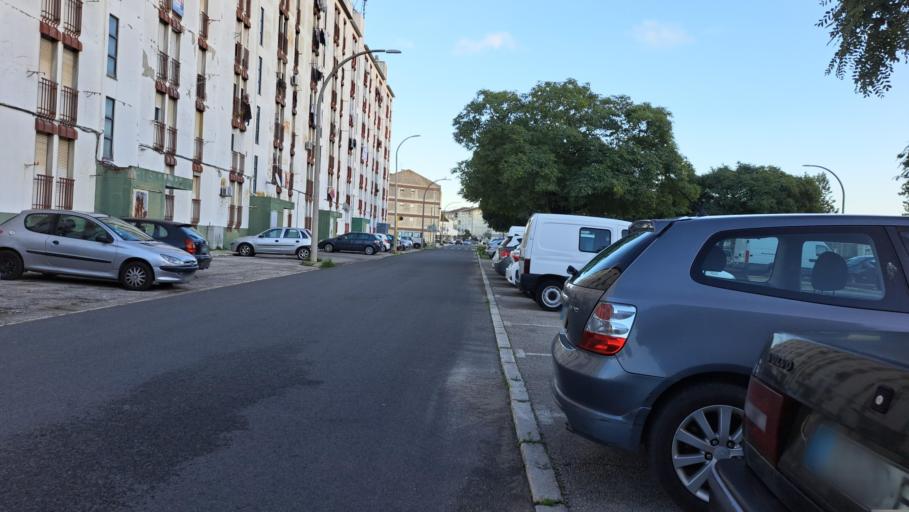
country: PT
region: Setubal
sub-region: Moita
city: Alhos Vedros
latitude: 38.6470
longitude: -9.0400
